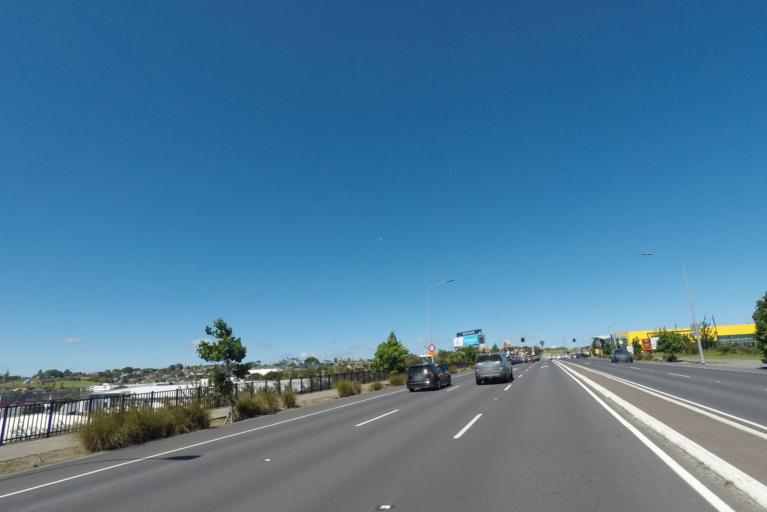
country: NZ
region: Auckland
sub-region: Auckland
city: Rosebank
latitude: -36.8201
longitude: 174.6109
